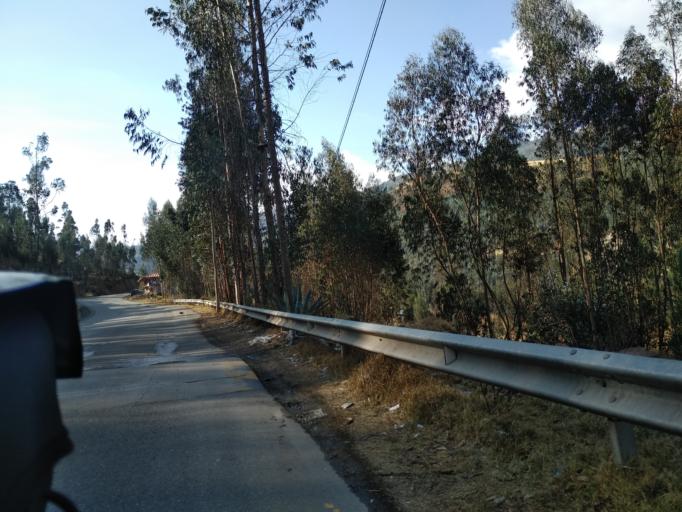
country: PE
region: La Libertad
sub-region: Provincia de Otuzco
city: Mache
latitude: -7.9985
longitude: -78.5081
